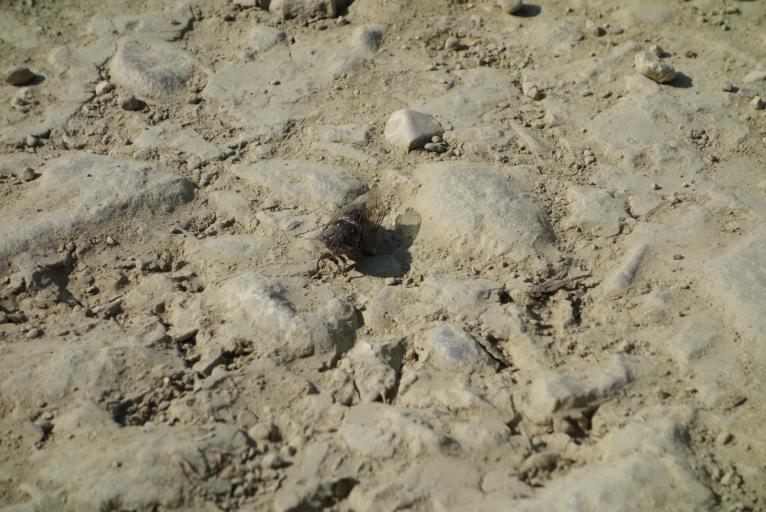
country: AL
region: Berat
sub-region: Rrethi i Skraparit
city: Cepan
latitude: 40.4235
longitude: 20.2940
